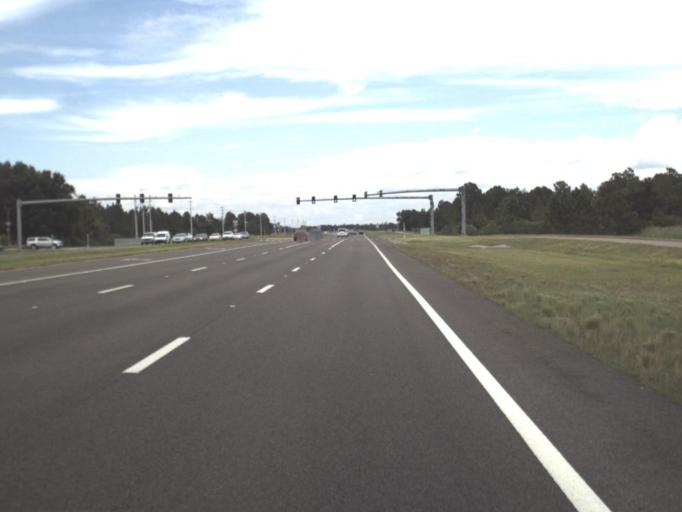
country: US
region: Florida
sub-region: Hillsborough County
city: Pebble Creek
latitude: 28.1876
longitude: -82.3460
